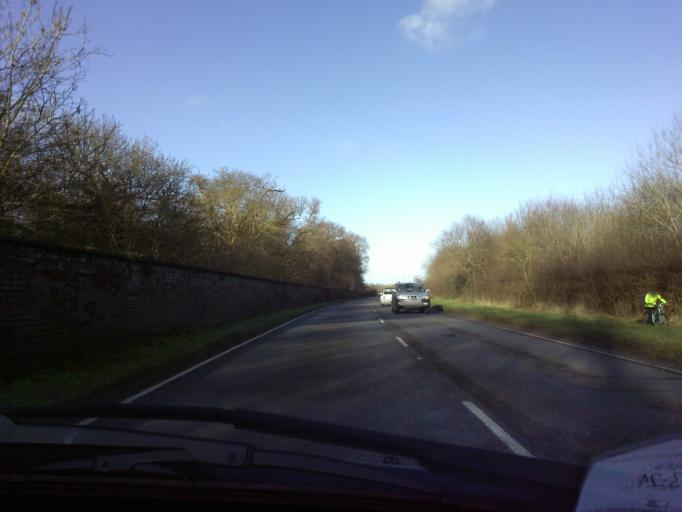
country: GB
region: England
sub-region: Hampshire
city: Romsey
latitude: 50.9825
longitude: -1.4868
